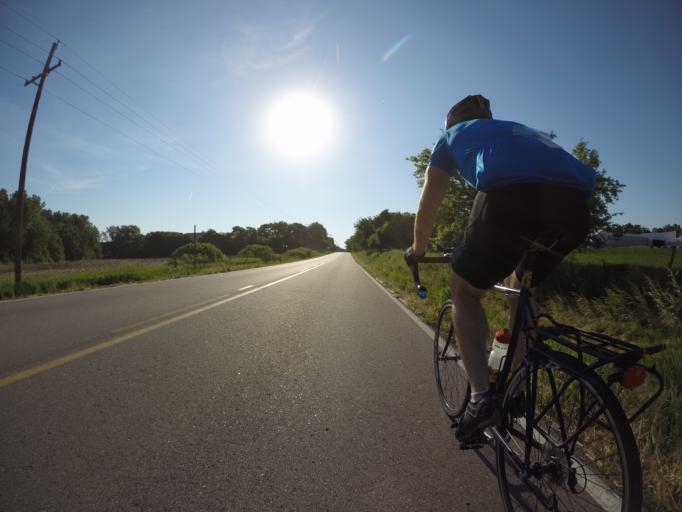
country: US
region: Nebraska
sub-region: Gage County
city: Wymore
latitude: 40.0883
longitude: -96.4873
